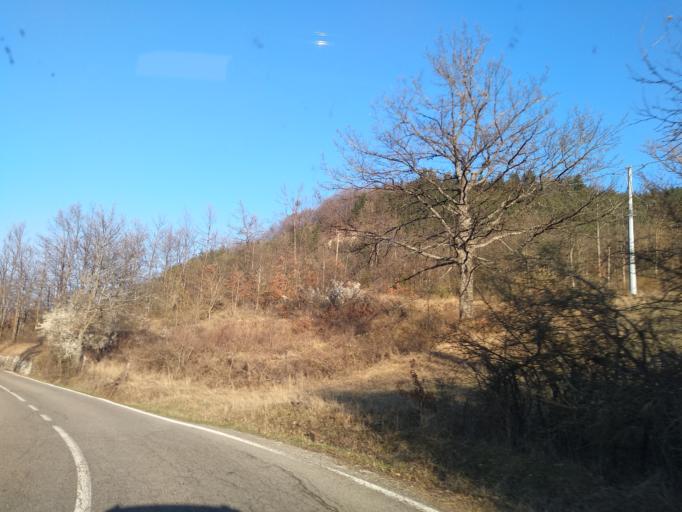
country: IT
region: Emilia-Romagna
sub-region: Provincia di Reggio Emilia
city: Ramiseto
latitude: 44.4140
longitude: 10.2927
